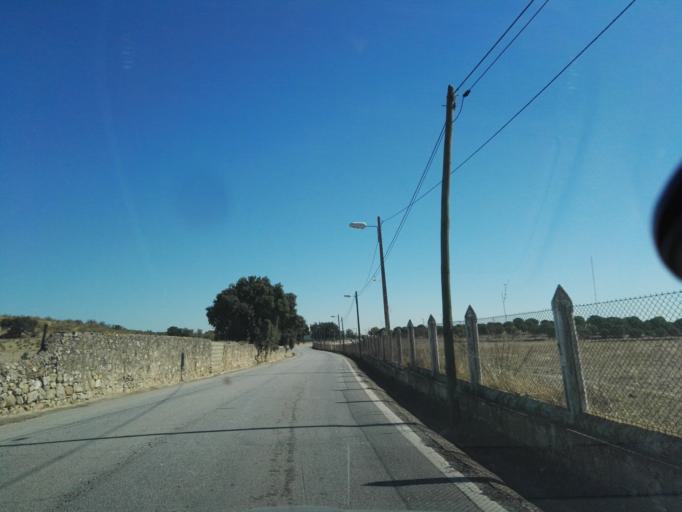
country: PT
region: Portalegre
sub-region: Elvas
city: Elvas
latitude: 38.8894
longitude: -7.1361
